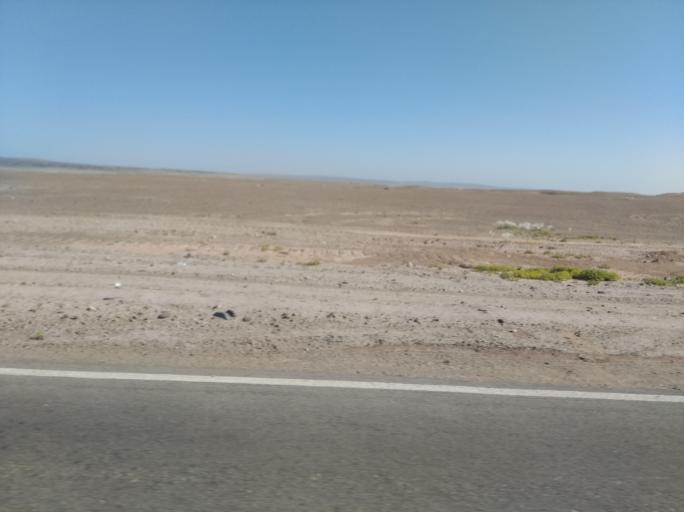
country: CL
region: Atacama
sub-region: Provincia de Copiapo
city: Copiapo
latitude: -27.3206
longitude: -70.8206
